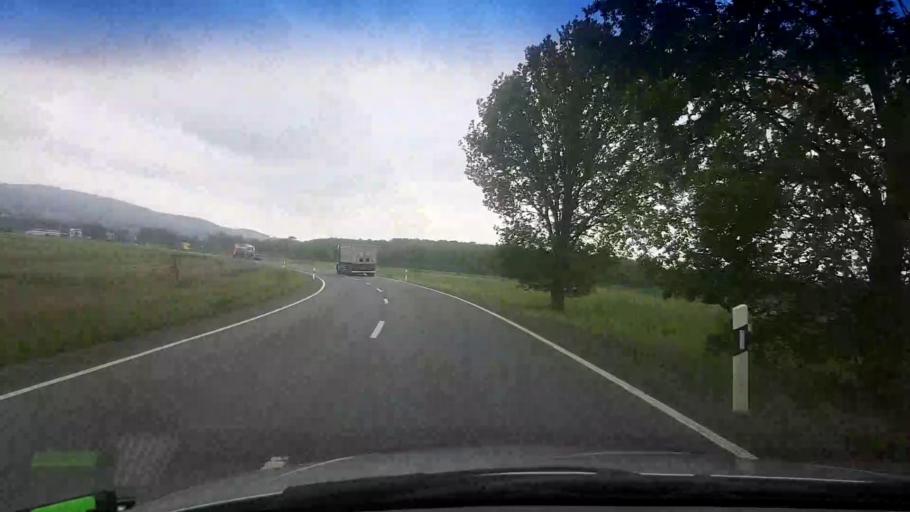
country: DE
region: Bavaria
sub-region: Upper Franconia
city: Gesees
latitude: 50.0182
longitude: 11.6642
